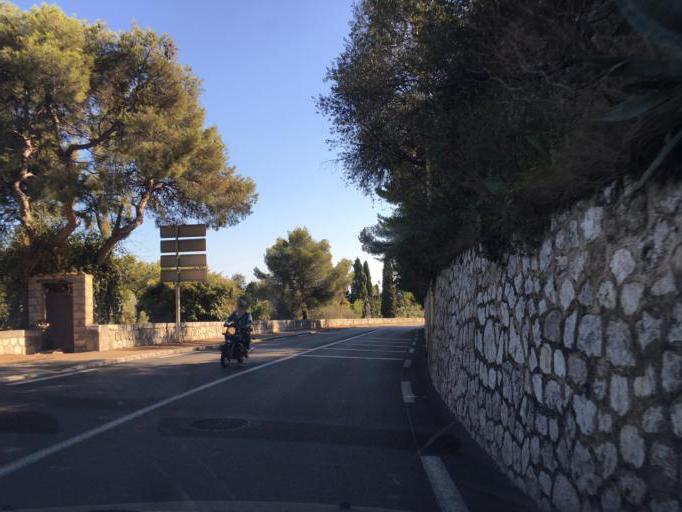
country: FR
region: Provence-Alpes-Cote d'Azur
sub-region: Departement des Alpes-Maritimes
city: Beaulieu-sur-Mer
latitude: 43.7115
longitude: 7.3199
